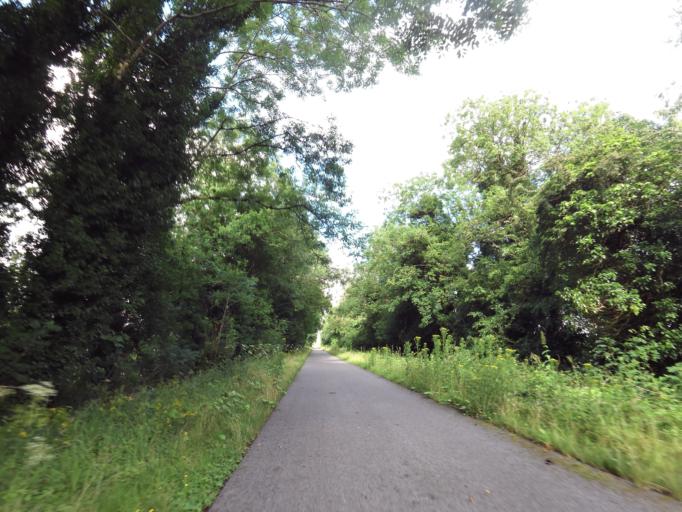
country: IE
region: Leinster
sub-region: An Iarmhi
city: Kilbeggan
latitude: 53.4392
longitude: -7.5593
